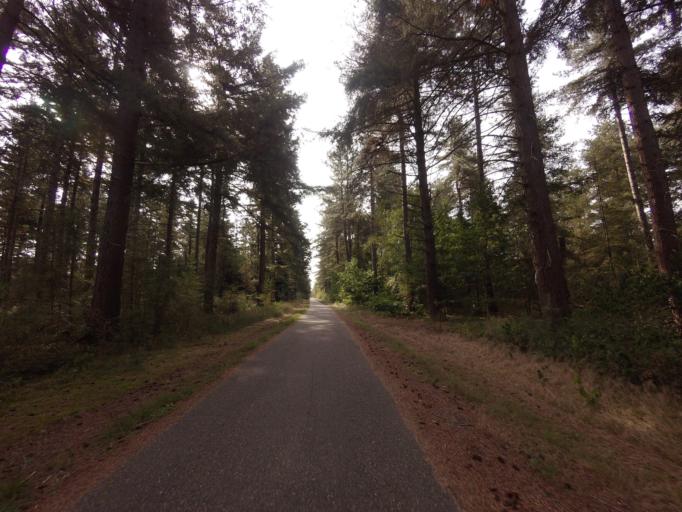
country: NL
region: North Brabant
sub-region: Gemeente Mill en Sint Hubert
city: Wilbertoord
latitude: 51.6103
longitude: 5.8184
